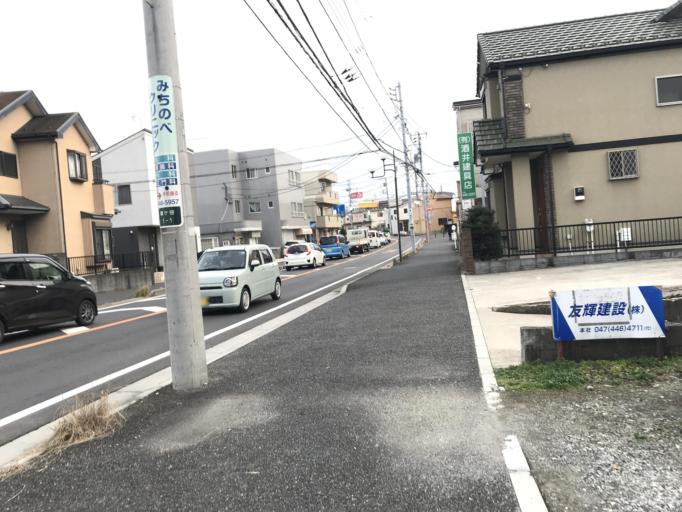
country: JP
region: Chiba
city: Shiroi
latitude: 35.7606
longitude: 140.0123
